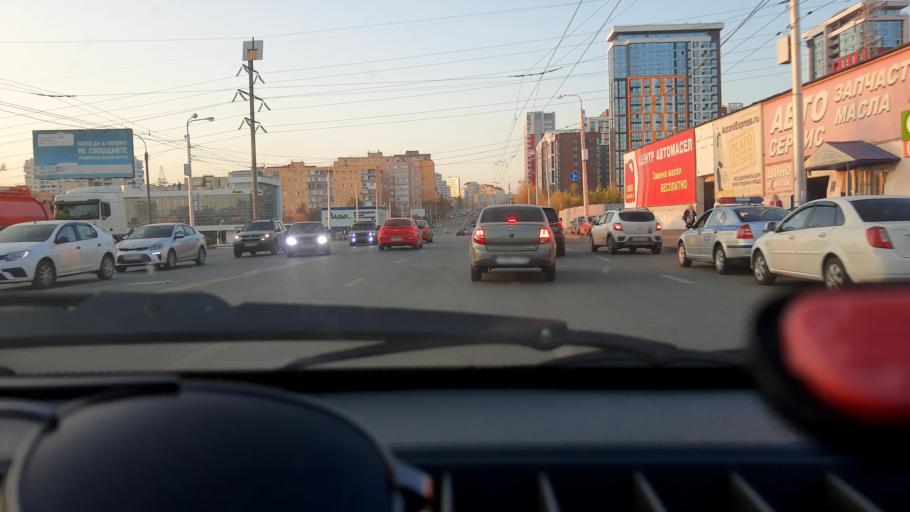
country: RU
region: Bashkortostan
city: Ufa
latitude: 54.7523
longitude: 56.0269
